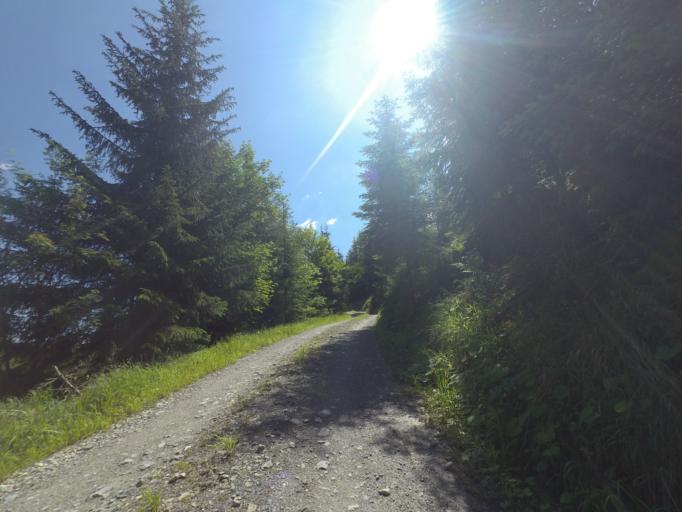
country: AT
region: Salzburg
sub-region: Politischer Bezirk Sankt Johann im Pongau
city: Schwarzach im Pongau
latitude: 47.3052
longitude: 13.1519
